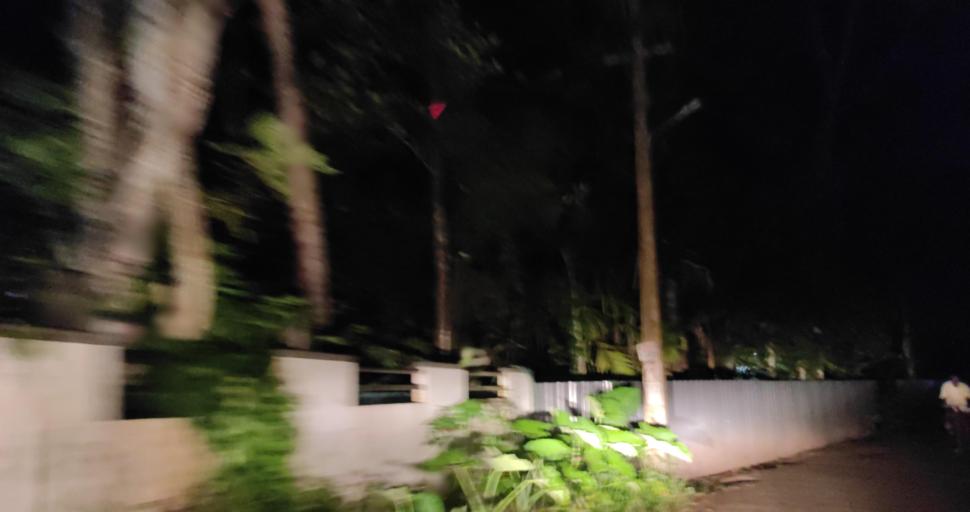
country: IN
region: Kerala
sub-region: Alappuzha
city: Shertallai
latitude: 9.6182
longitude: 76.3364
